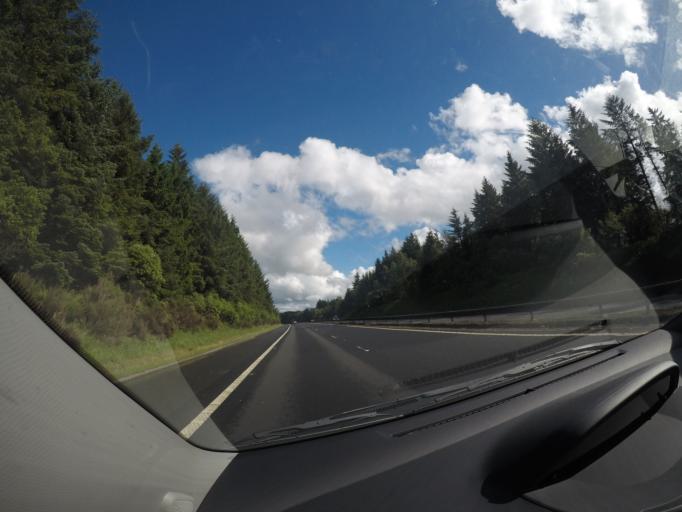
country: GB
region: Scotland
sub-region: South Lanarkshire
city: Douglas
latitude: 55.5876
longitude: -3.8282
